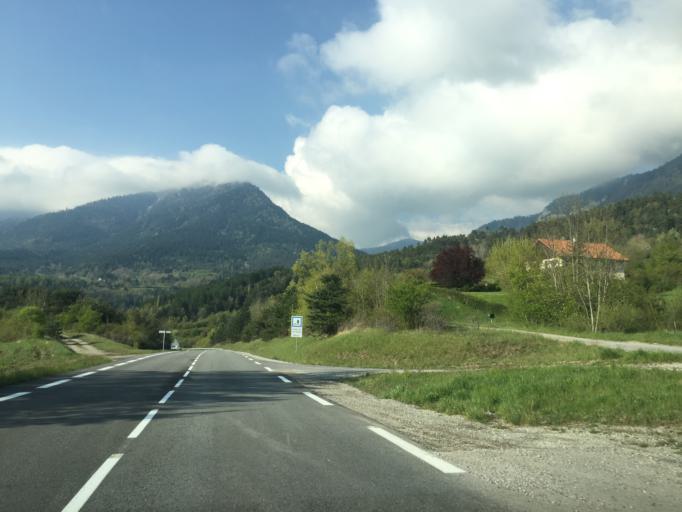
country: FR
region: Rhone-Alpes
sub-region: Departement de l'Isere
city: Mens
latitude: 44.7939
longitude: 5.6350
